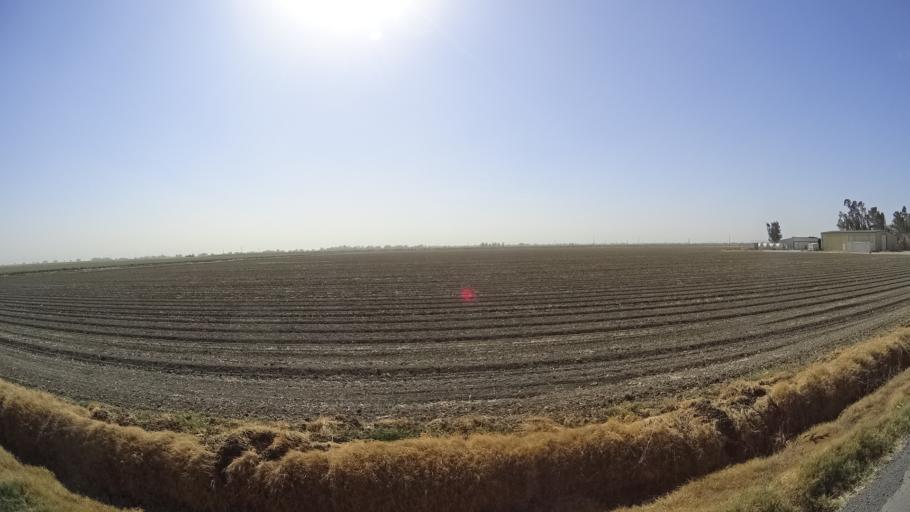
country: US
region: California
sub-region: Yolo County
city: Davis
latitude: 38.5750
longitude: -121.6803
